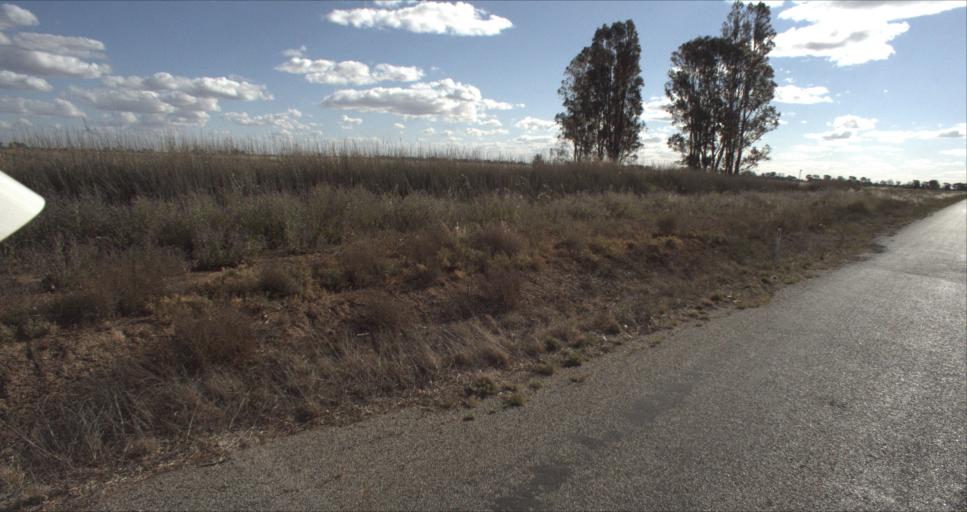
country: AU
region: New South Wales
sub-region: Leeton
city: Leeton
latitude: -34.4421
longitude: 146.2390
